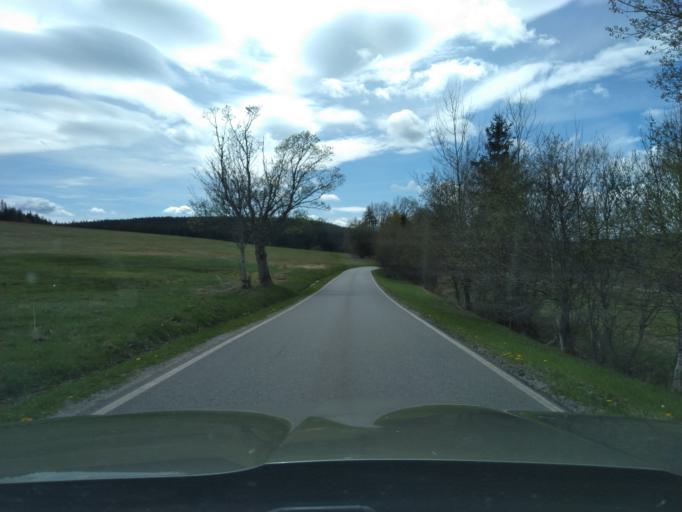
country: CZ
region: Jihocesky
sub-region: Okres Prachatice
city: Zdikov
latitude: 49.0439
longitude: 13.6695
